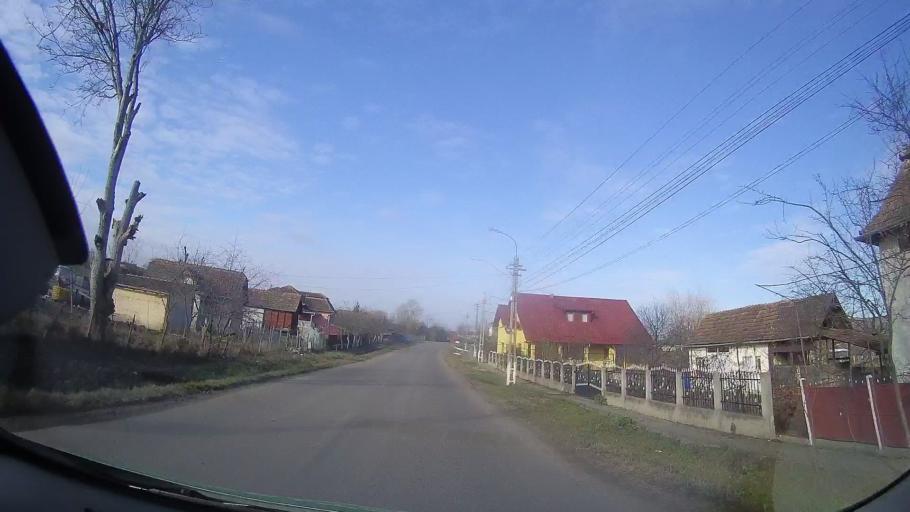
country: RO
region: Mures
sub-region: Comuna Valea Larga
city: Valea Larga
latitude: 46.6164
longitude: 24.0819
